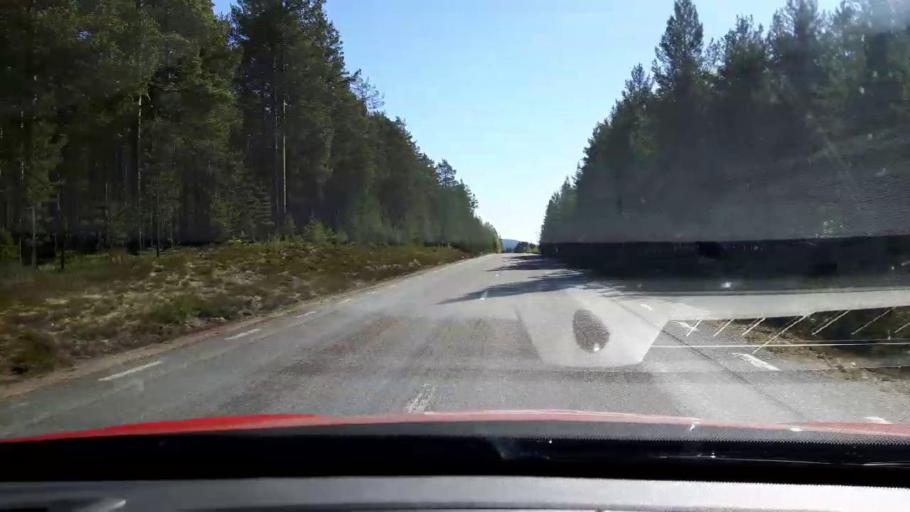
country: SE
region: Jaemtland
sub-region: Harjedalens Kommun
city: Sveg
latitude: 62.3069
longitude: 14.0479
